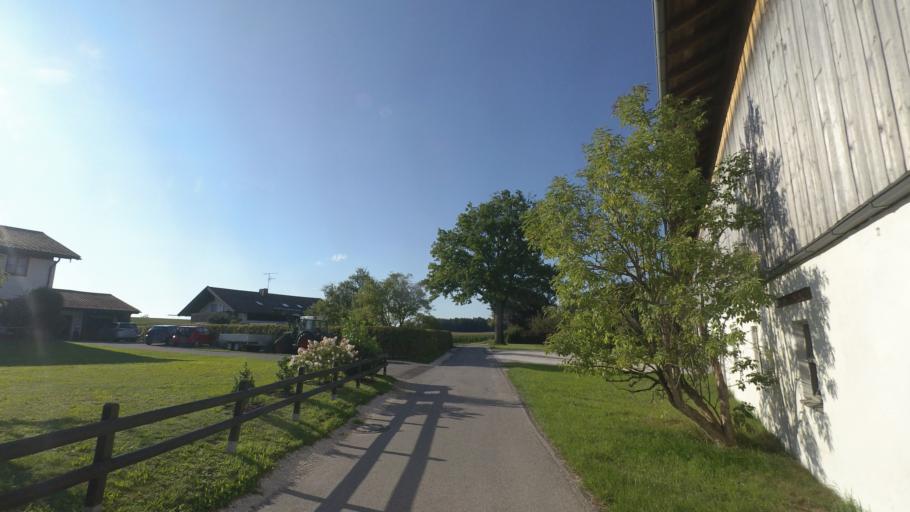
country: DE
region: Bavaria
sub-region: Upper Bavaria
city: Chieming
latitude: 47.8733
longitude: 12.5409
